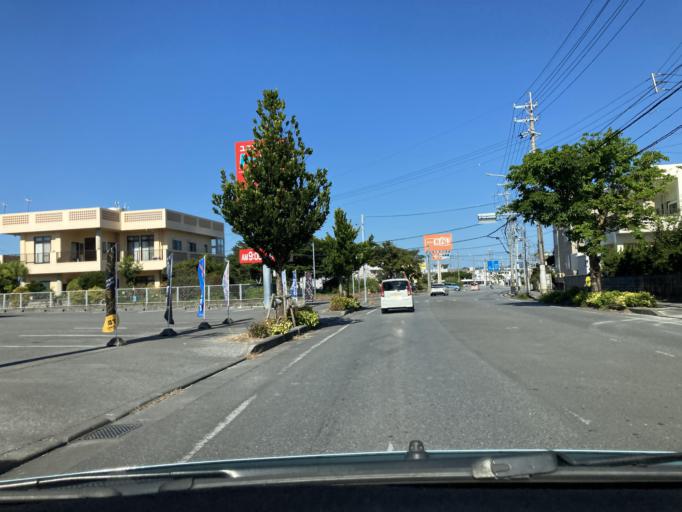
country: JP
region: Okinawa
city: Gushikawa
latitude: 26.3704
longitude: 127.8597
